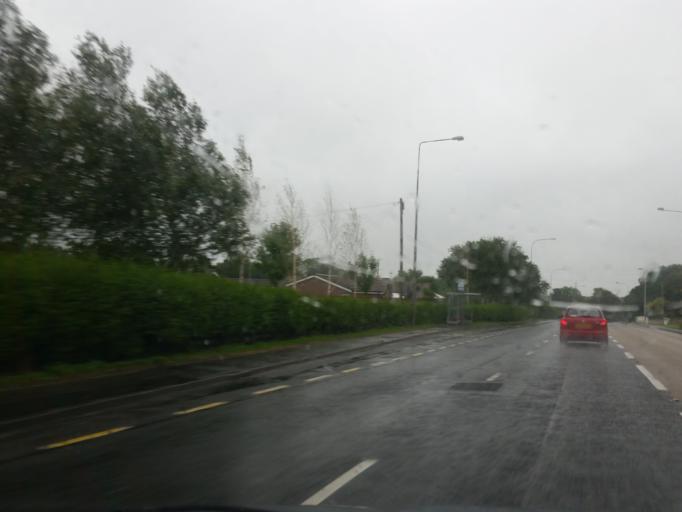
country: GB
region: Northern Ireland
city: Holywood
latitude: 54.6566
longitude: -5.7621
